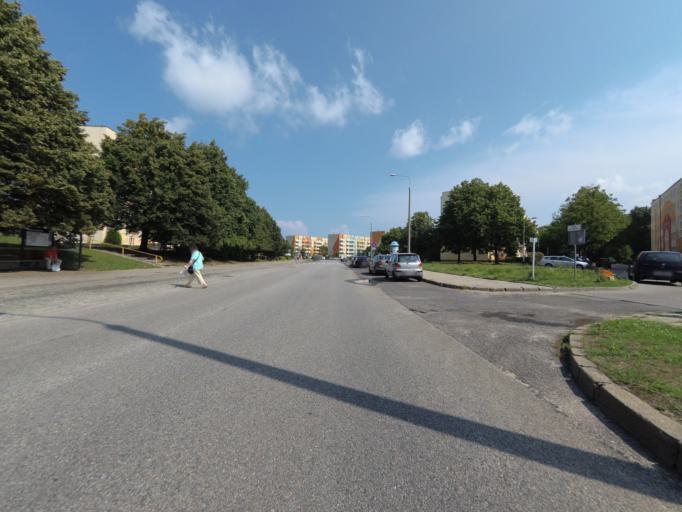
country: PL
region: Pomeranian Voivodeship
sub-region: Gdynia
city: Wielki Kack
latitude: 54.4917
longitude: 18.5108
